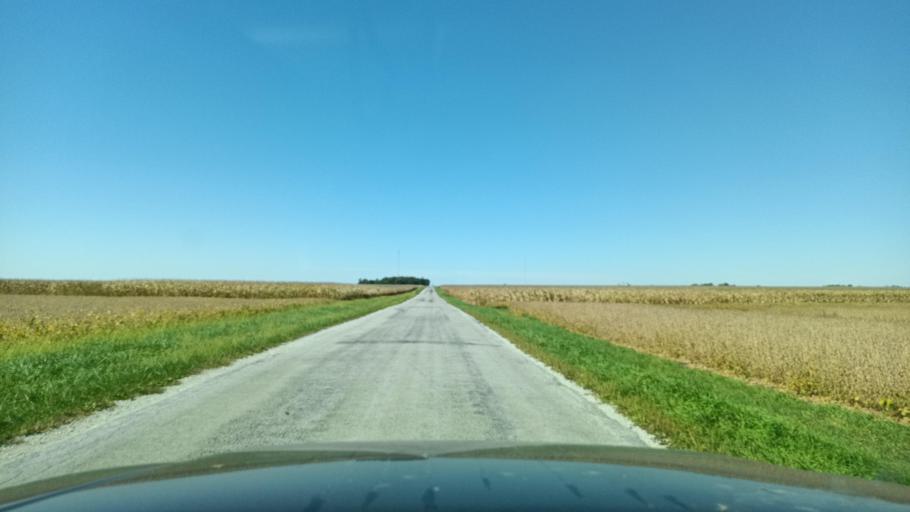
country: US
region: Illinois
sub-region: Champaign County
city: Mahomet
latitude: 40.0987
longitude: -88.3828
